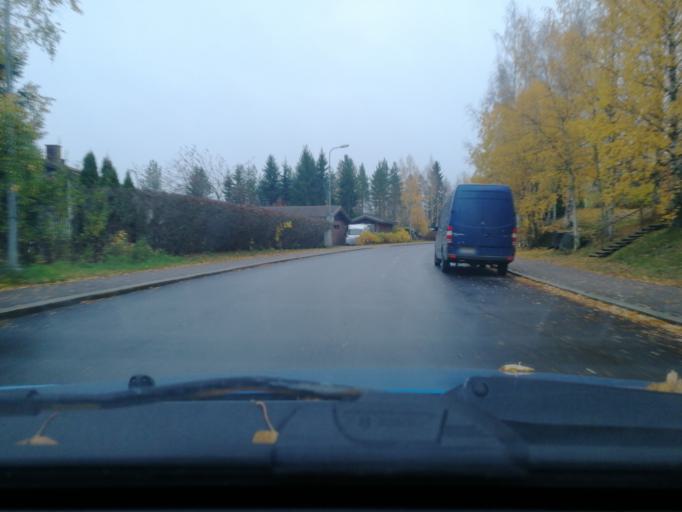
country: FI
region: Pirkanmaa
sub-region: Tampere
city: Tampere
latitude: 61.4444
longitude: 23.8727
